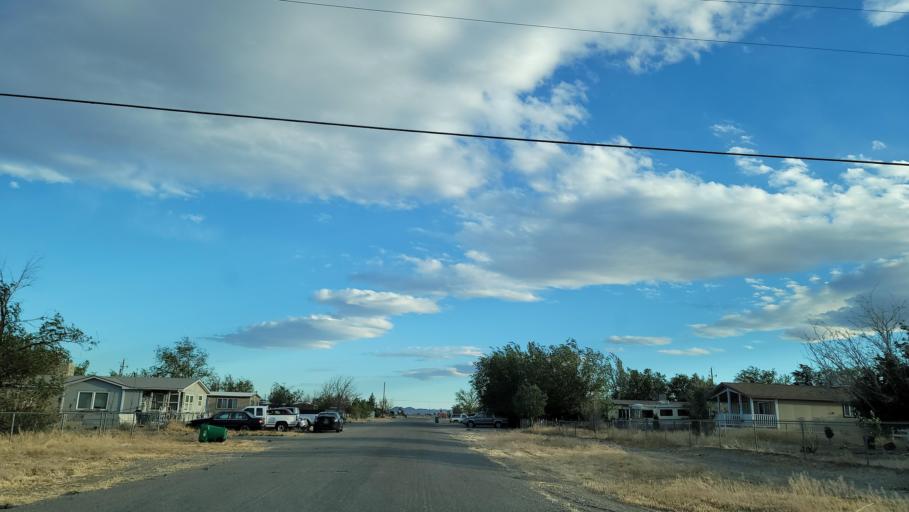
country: US
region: Nevada
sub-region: Lyon County
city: Silver Springs
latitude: 39.4072
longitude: -119.2224
